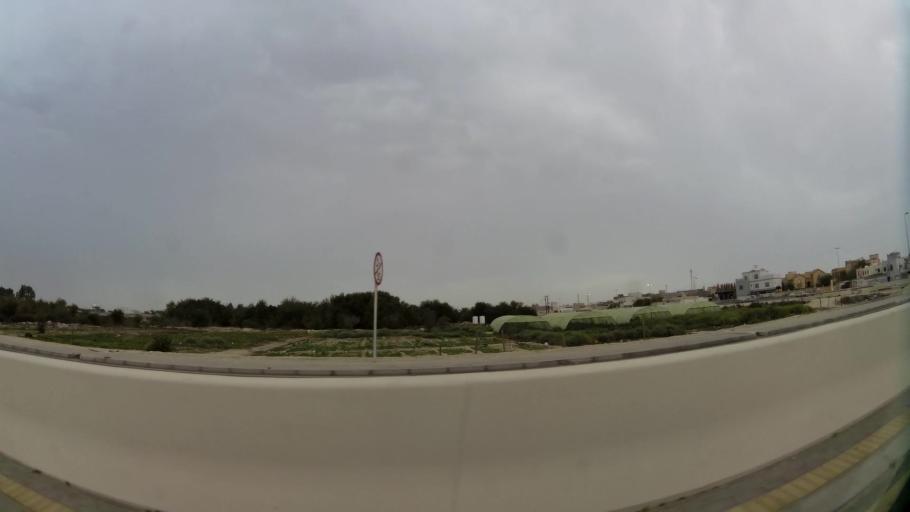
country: BH
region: Central Governorate
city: Dar Kulayb
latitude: 26.0833
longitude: 50.5012
